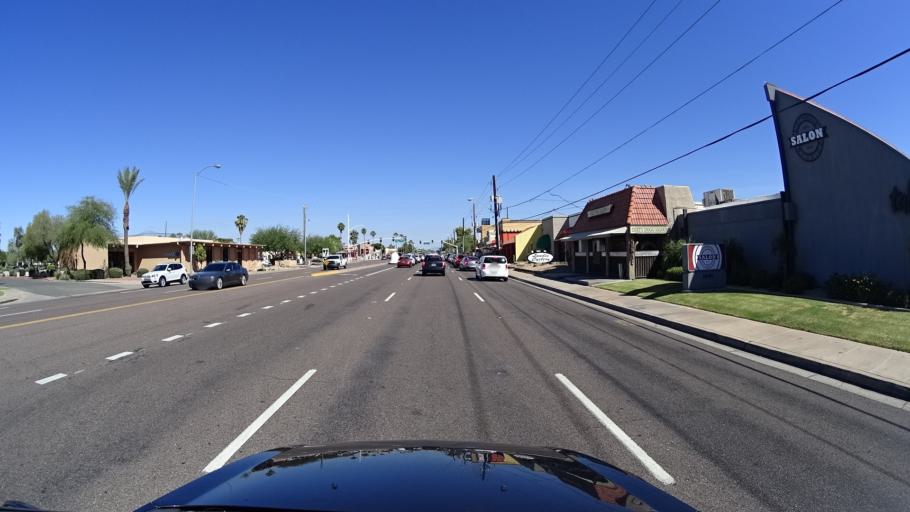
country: US
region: Arizona
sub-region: Maricopa County
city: Paradise Valley
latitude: 33.5809
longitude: -111.9259
